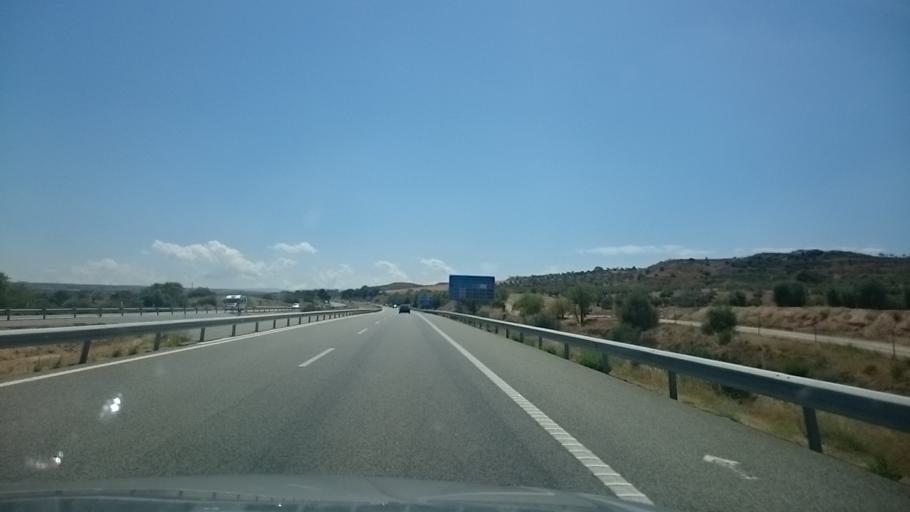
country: ES
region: Catalonia
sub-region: Provincia de Lleida
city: Juneda
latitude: 41.5019
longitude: 0.8467
